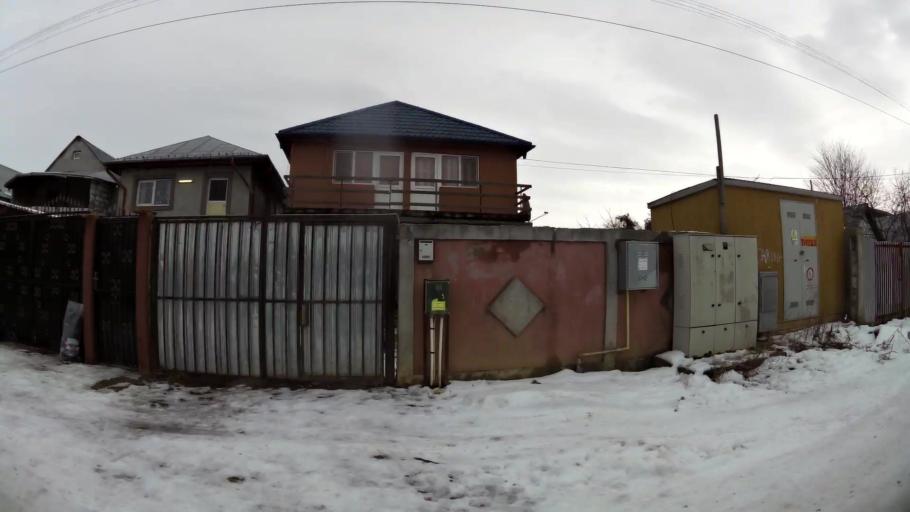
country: RO
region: Ilfov
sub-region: Comuna Pantelimon
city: Pantelimon
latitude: 44.4607
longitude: 26.2014
